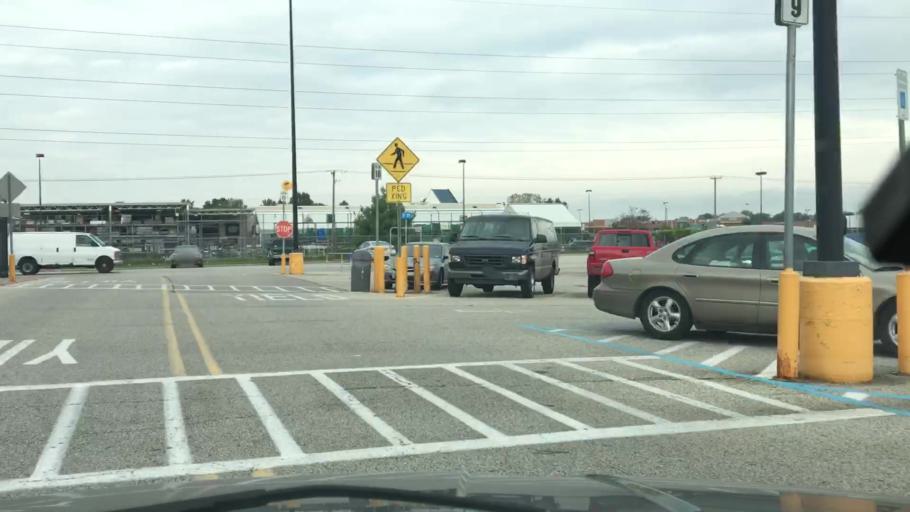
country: US
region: Michigan
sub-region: Berrien County
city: Fair Plain
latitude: 42.0783
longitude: -86.4250
